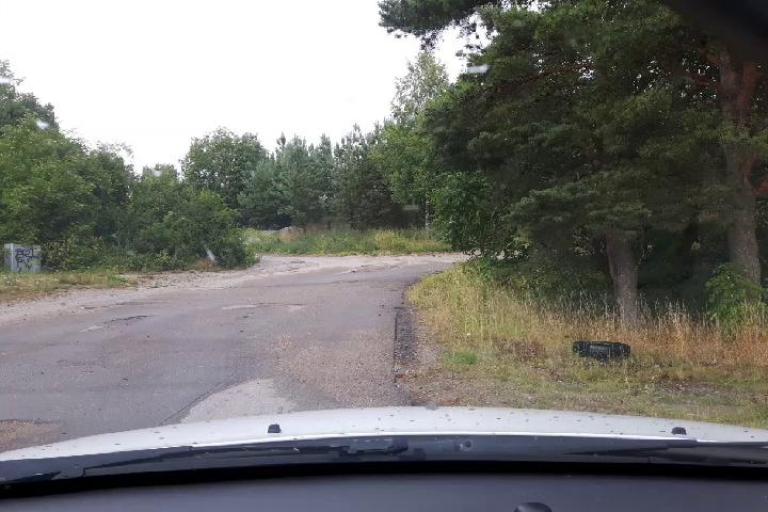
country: SE
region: Uppsala
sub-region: Uppsala Kommun
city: Gamla Uppsala
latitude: 59.8847
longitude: 17.6199
